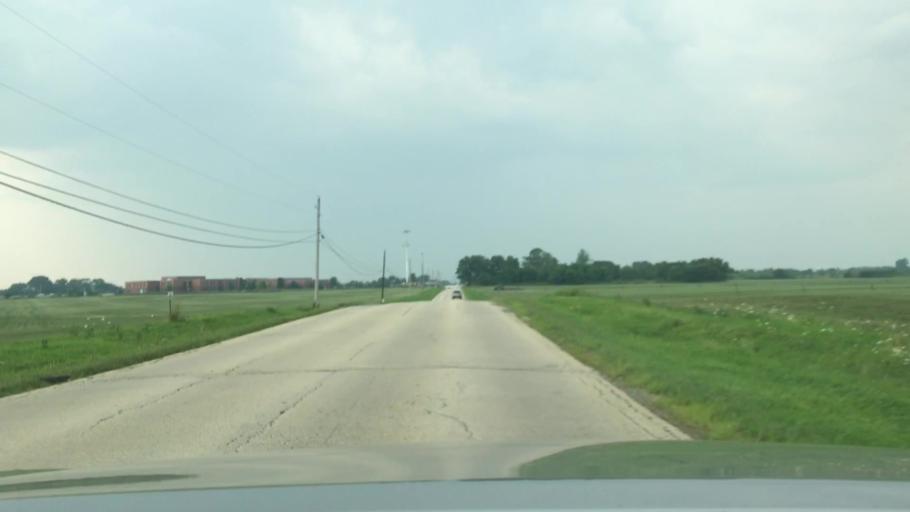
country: US
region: Illinois
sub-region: Will County
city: Plainfield
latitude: 41.6884
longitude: -88.2537
